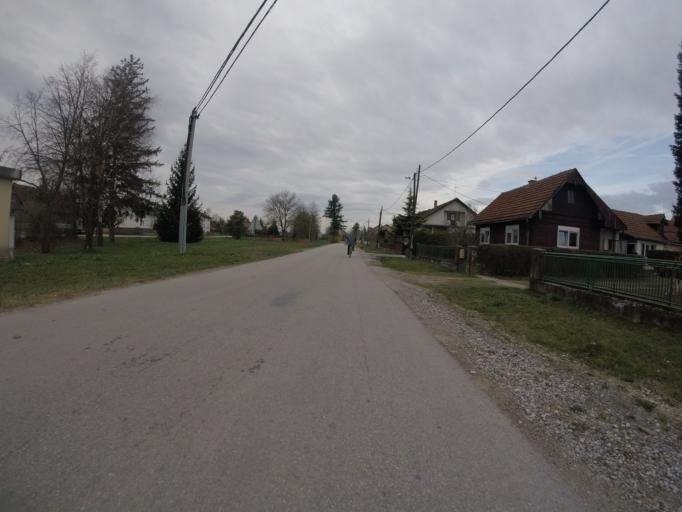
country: HR
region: Zagrebacka
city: Lukavec
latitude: 45.7002
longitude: 15.9964
